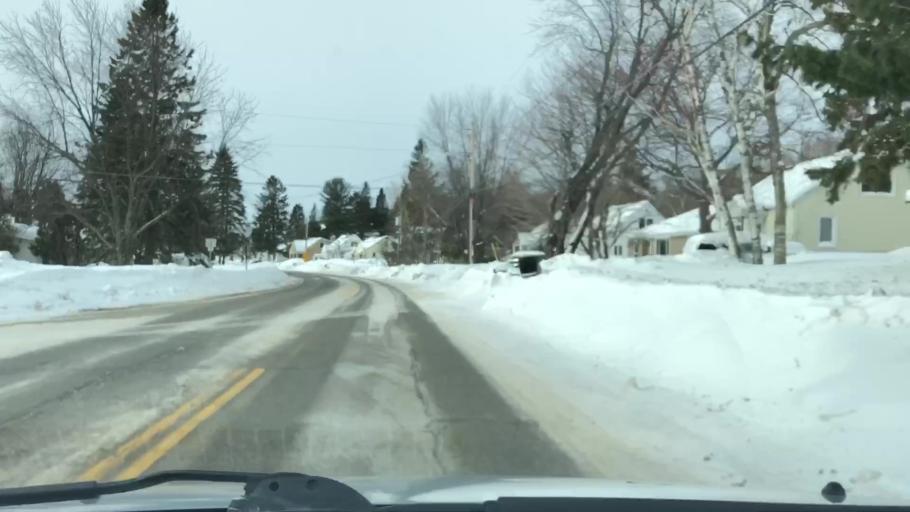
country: US
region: Minnesota
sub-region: Saint Louis County
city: Duluth
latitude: 46.7990
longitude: -92.1468
